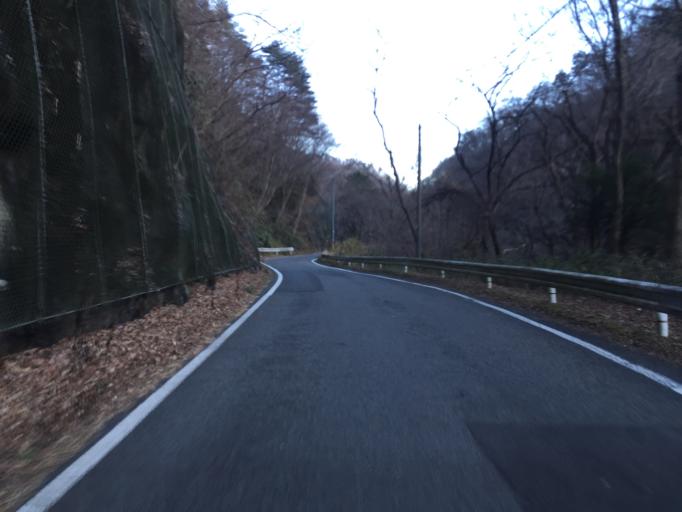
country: JP
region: Fukushima
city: Iwaki
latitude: 37.1990
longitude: 140.7787
